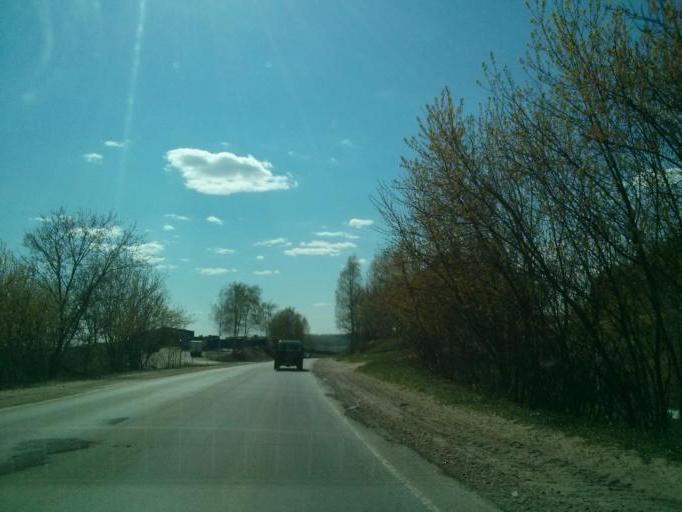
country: RU
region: Nizjnij Novgorod
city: Pavlovo
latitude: 55.9386
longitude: 43.0930
